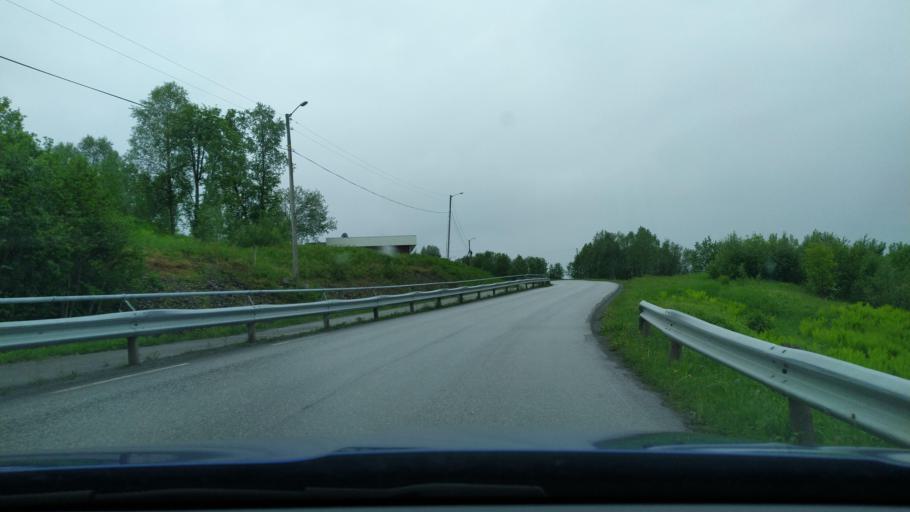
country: NO
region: Troms
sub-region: Dyroy
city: Brostadbotn
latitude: 69.0859
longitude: 17.6959
